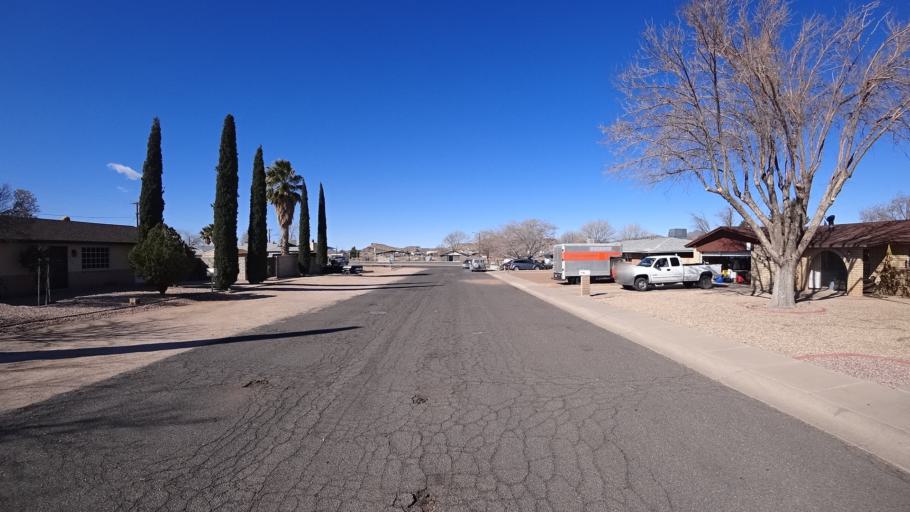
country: US
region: Arizona
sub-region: Mohave County
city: Kingman
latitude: 35.1949
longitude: -114.0215
